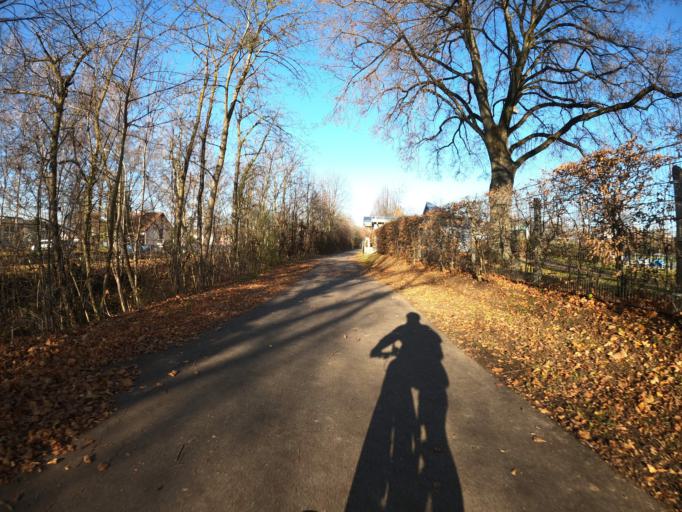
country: DE
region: Baden-Wuerttemberg
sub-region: Regierungsbezirk Stuttgart
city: Goeppingen
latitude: 48.6954
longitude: 9.6693
